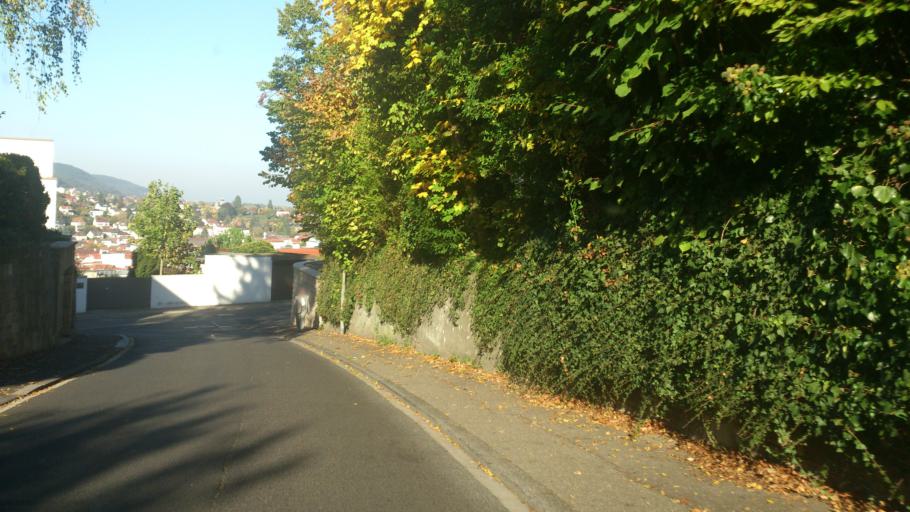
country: DE
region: Rheinland-Pfalz
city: Neustadt
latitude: 49.3479
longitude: 8.1344
